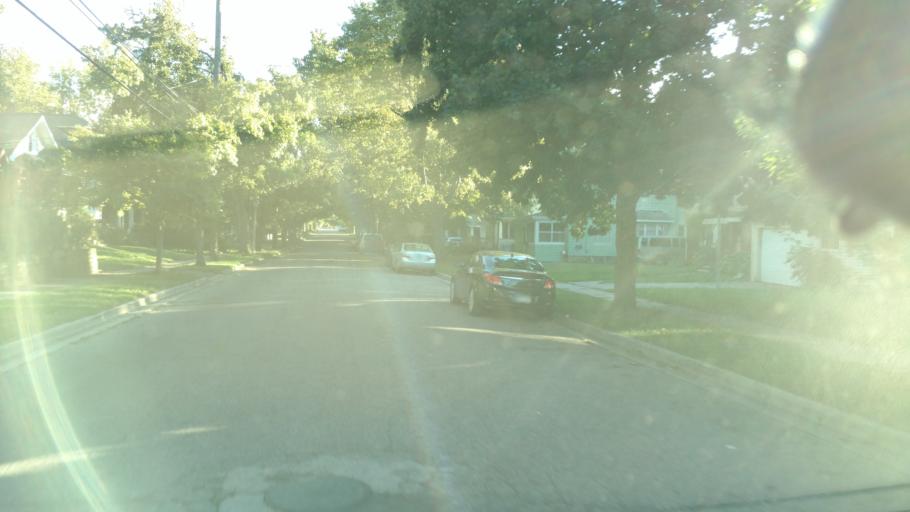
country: US
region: Michigan
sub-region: Ingham County
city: Lansing
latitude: 42.7327
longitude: -84.5213
